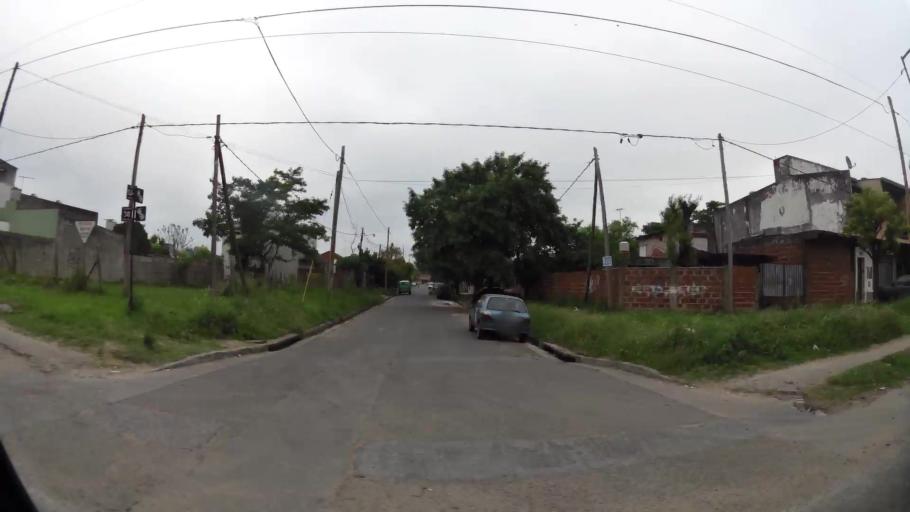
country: AR
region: Buenos Aires
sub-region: Partido de La Plata
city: La Plata
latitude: -34.9318
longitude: -57.9908
